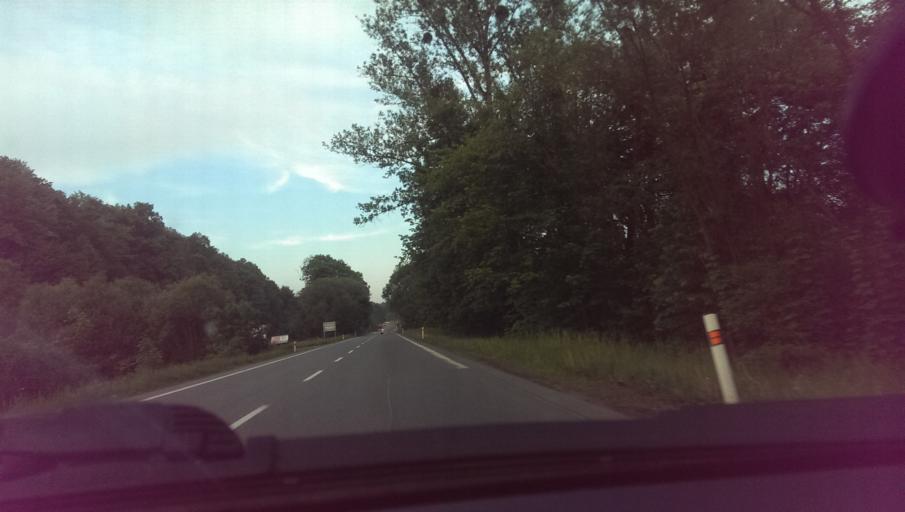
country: CZ
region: Zlin
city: Valasske Mezirici
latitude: 49.4762
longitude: 17.9961
